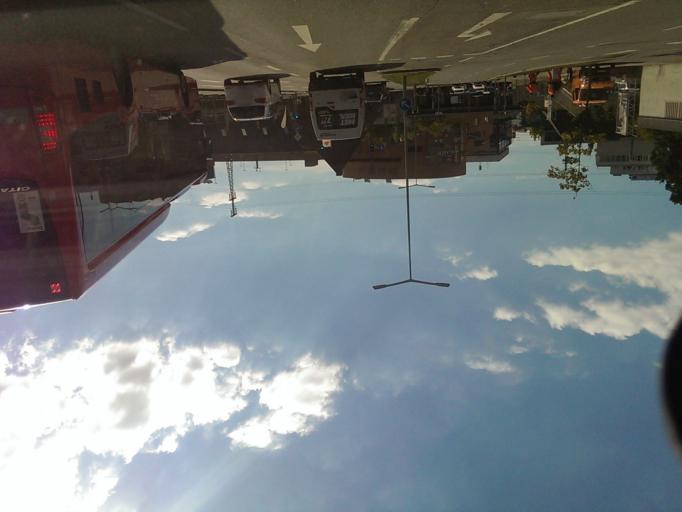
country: DE
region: Baden-Wuerttemberg
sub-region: Regierungsbezirk Stuttgart
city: Boeblingen
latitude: 48.6906
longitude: 9.0056
